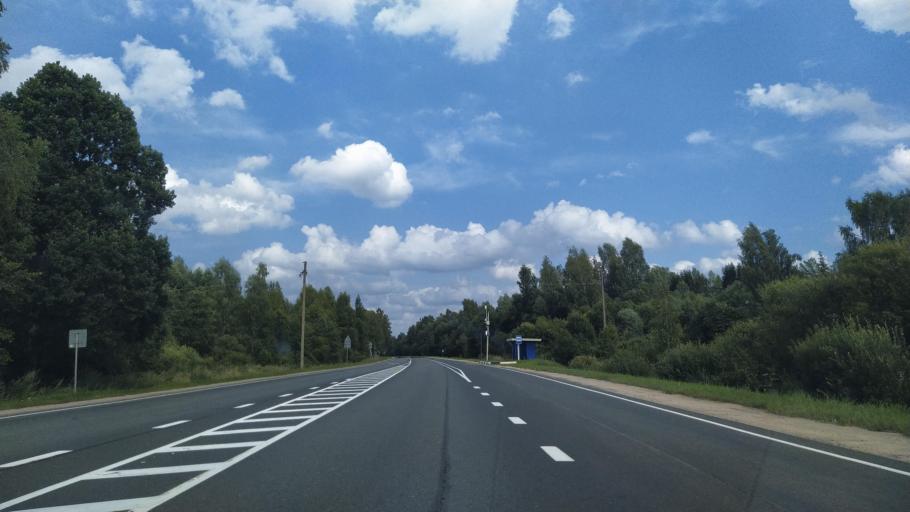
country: RU
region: Pskov
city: Dno
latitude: 57.9935
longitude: 29.8496
